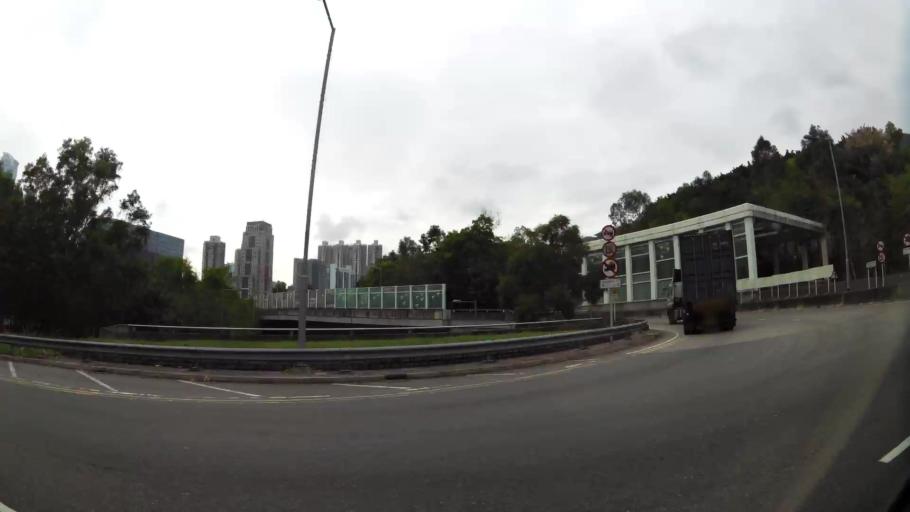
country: HK
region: Tsuen Wan
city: Tsuen Wan
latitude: 22.3754
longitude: 114.1199
